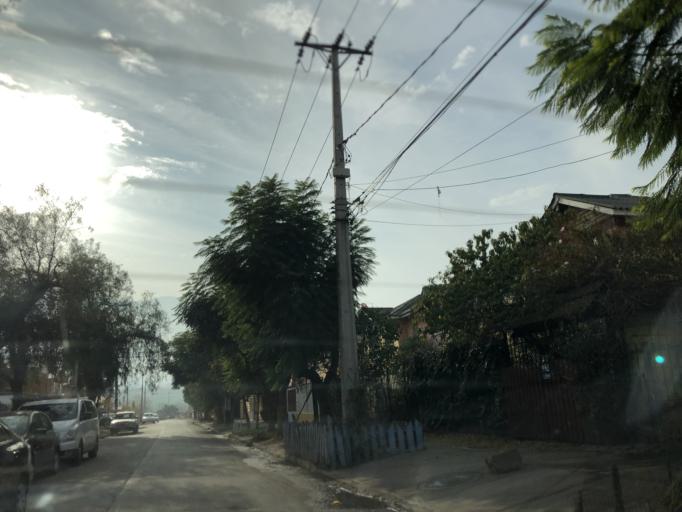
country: CL
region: Santiago Metropolitan
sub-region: Provincia de Cordillera
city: Puente Alto
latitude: -33.5858
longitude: -70.5499
